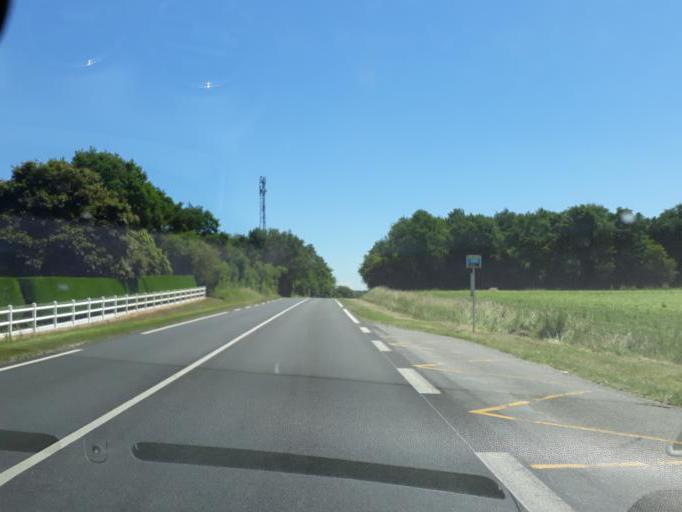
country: FR
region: Centre
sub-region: Departement du Cher
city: Vignoux-sur-Barangeon
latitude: 47.2063
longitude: 2.1564
